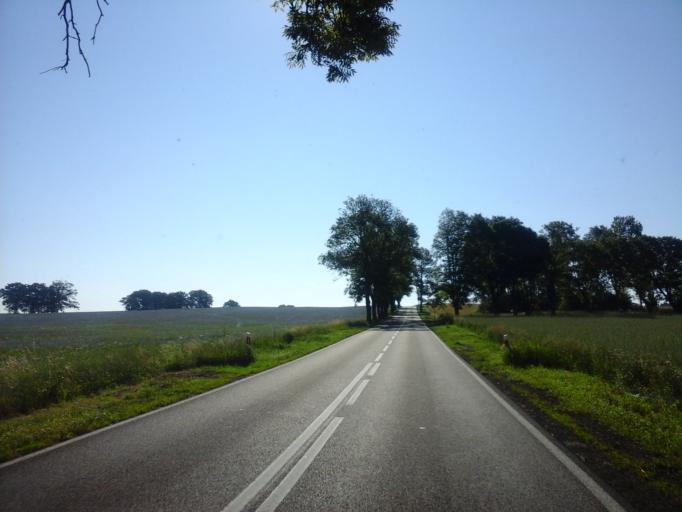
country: PL
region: West Pomeranian Voivodeship
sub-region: Powiat lobeski
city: Wegorzyno
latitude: 53.4987
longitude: 15.6721
